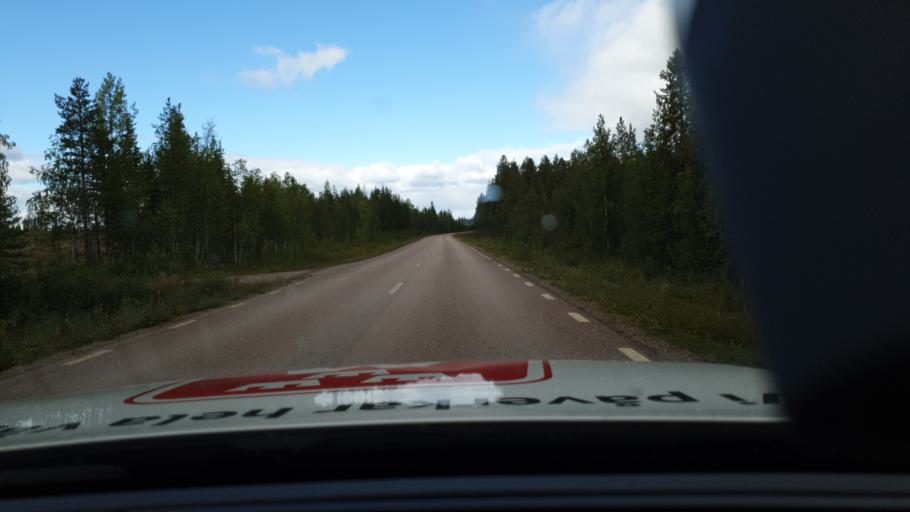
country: SE
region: Norrbotten
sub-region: Pajala Kommun
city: Pajala
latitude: 67.2293
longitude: 22.7841
